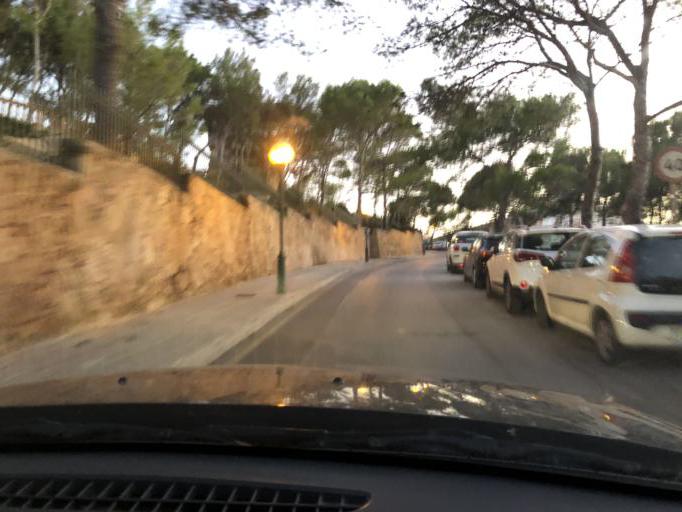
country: ES
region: Balearic Islands
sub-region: Illes Balears
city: Santa Ponsa
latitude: 39.5209
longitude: 2.4681
